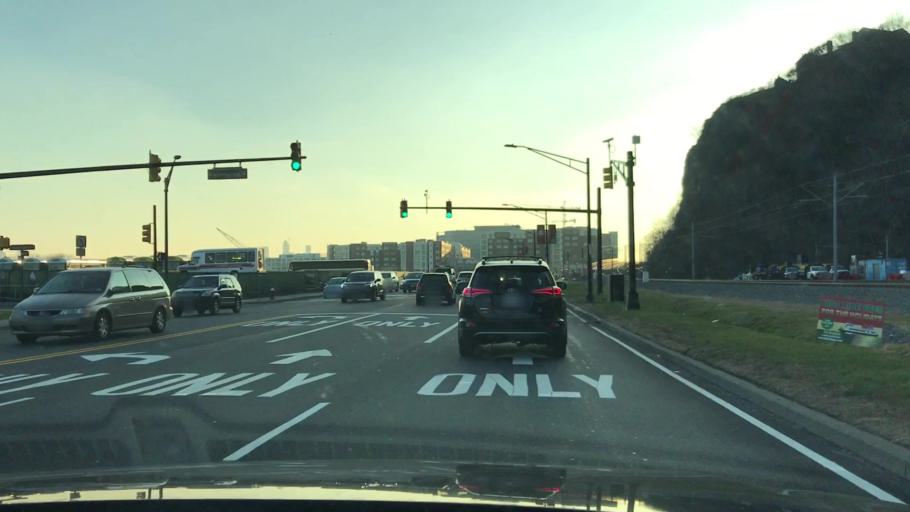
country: US
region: New Jersey
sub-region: Hudson County
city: Weehawken
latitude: 40.7667
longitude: -74.0189
